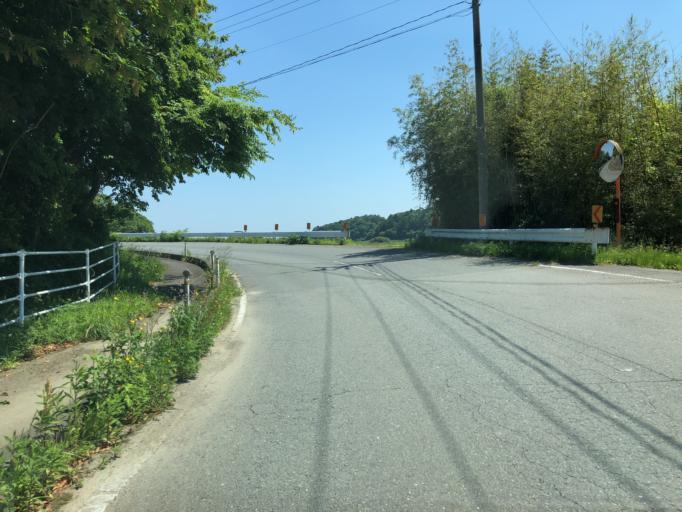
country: JP
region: Fukushima
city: Iwaki
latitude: 37.2275
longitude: 140.9969
